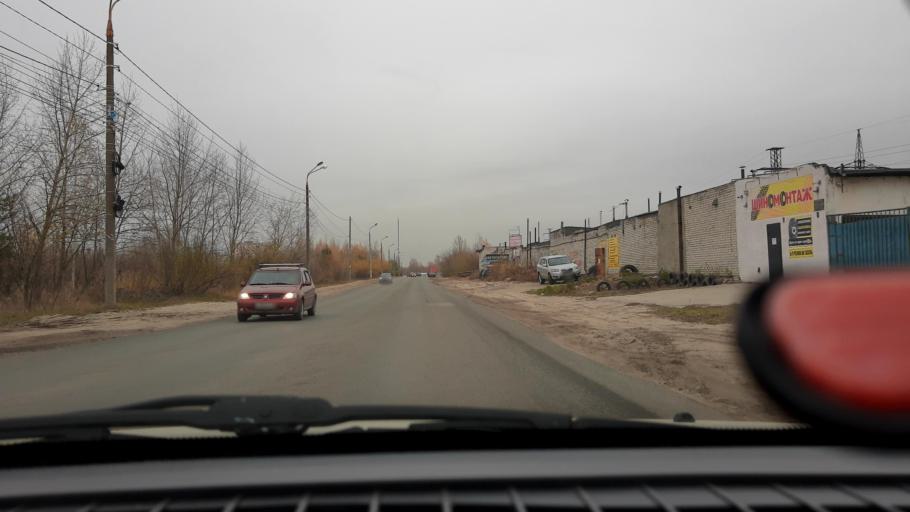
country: RU
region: Nizjnij Novgorod
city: Gorbatovka
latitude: 56.3595
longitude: 43.7992
